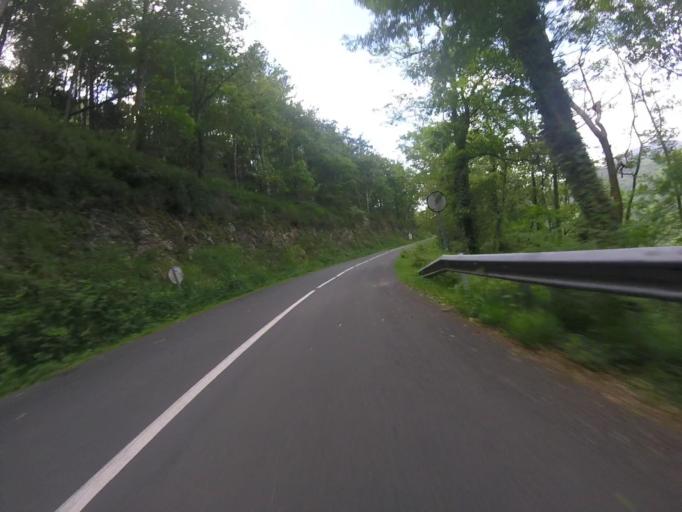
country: ES
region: Navarre
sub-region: Provincia de Navarra
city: Arano
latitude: 43.2585
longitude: -1.8500
